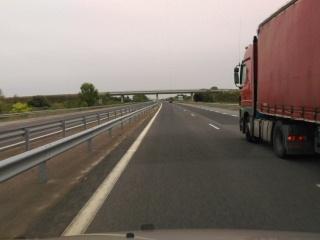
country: BG
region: Stara Zagora
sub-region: Obshtina Stara Zagora
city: Stara Zagora
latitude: 42.3290
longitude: 25.6277
